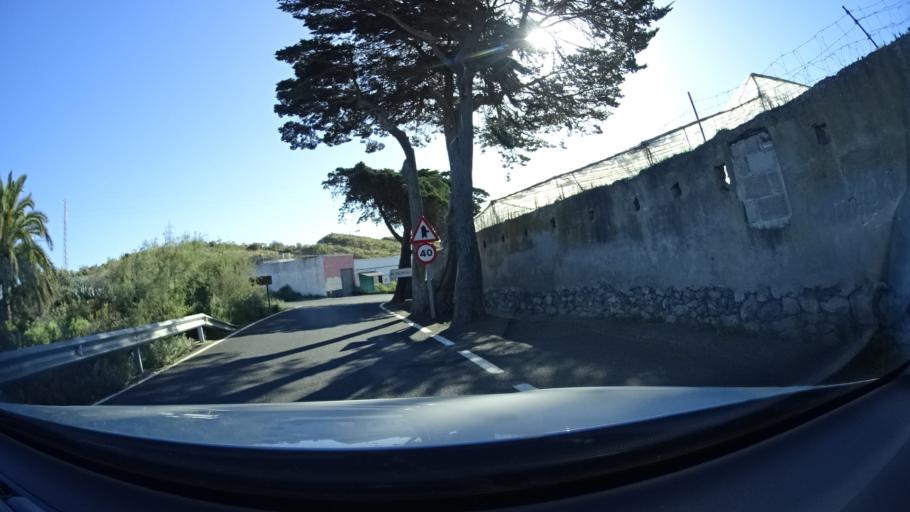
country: ES
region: Canary Islands
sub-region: Provincia de Las Palmas
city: Telde
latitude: 28.0184
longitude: -15.4572
